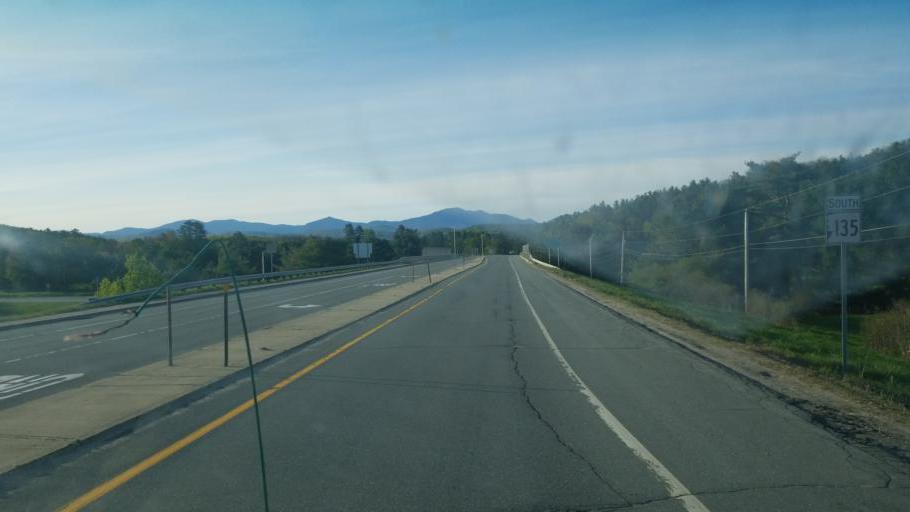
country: US
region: New Hampshire
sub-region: Grafton County
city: Littleton
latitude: 44.3266
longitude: -71.8073
